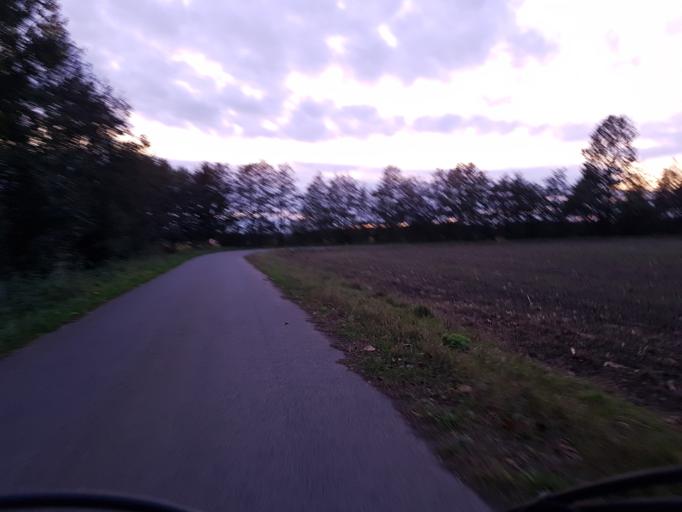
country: DE
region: Brandenburg
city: Schilda
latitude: 51.6233
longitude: 13.3444
